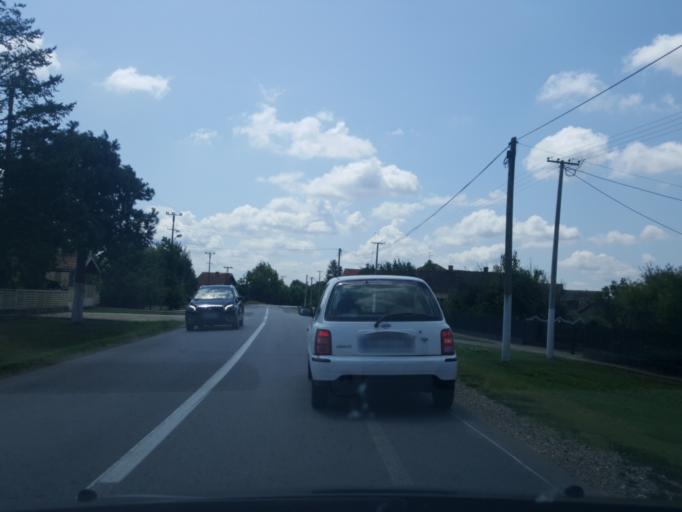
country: RS
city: Salas Nocajski
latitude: 44.9373
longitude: 19.5719
